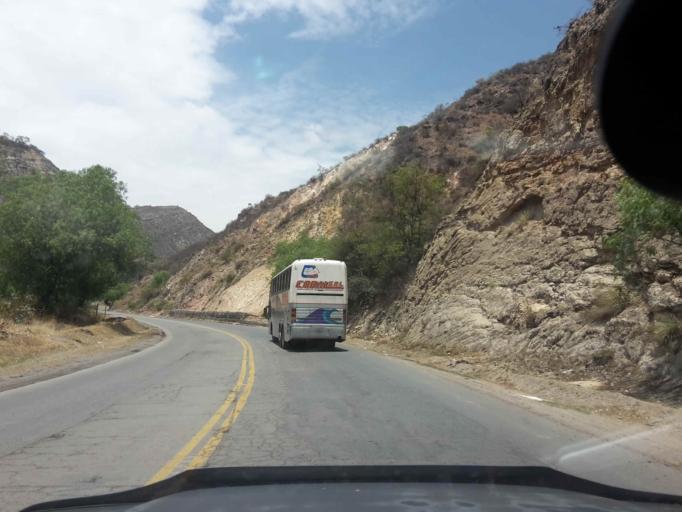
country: BO
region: Cochabamba
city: Sipe Sipe
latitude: -17.5306
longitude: -66.3358
